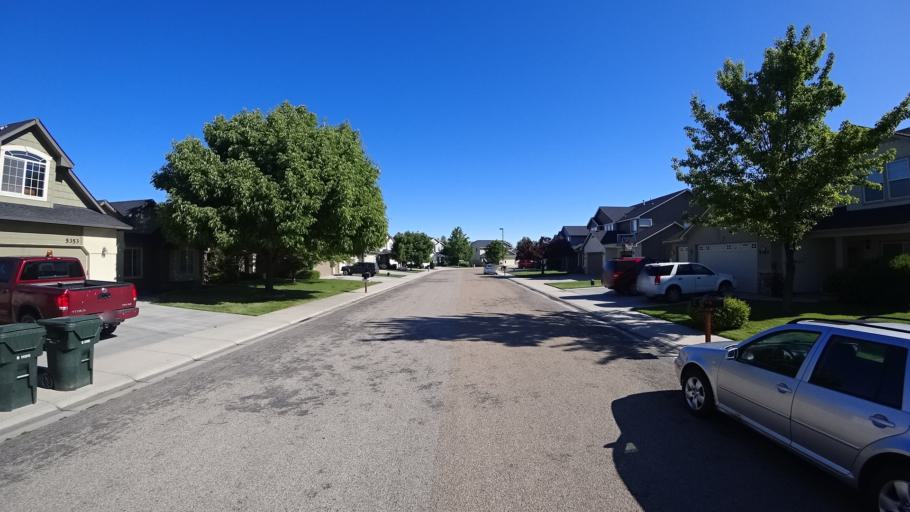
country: US
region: Idaho
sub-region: Ada County
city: Meridian
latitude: 43.6535
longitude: -116.4302
